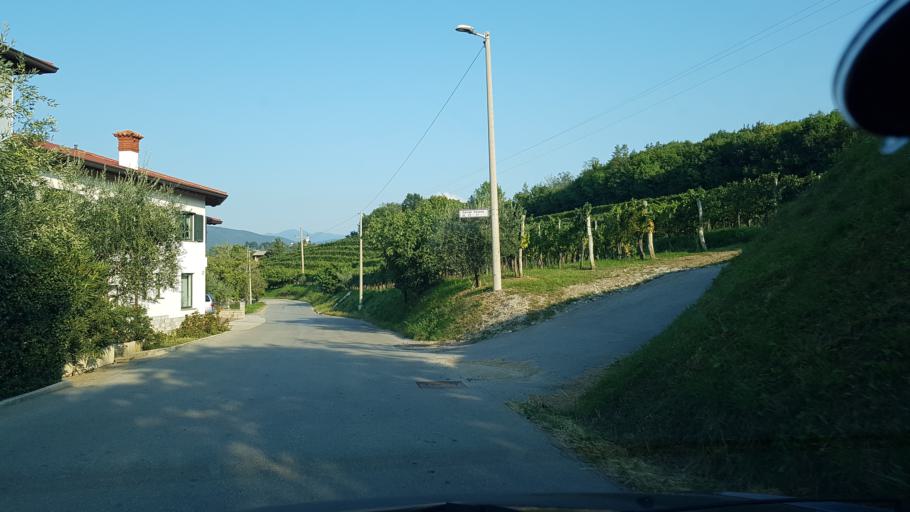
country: IT
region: Friuli Venezia Giulia
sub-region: Provincia di Gorizia
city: San Floriano del Collio
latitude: 45.9829
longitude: 13.5676
